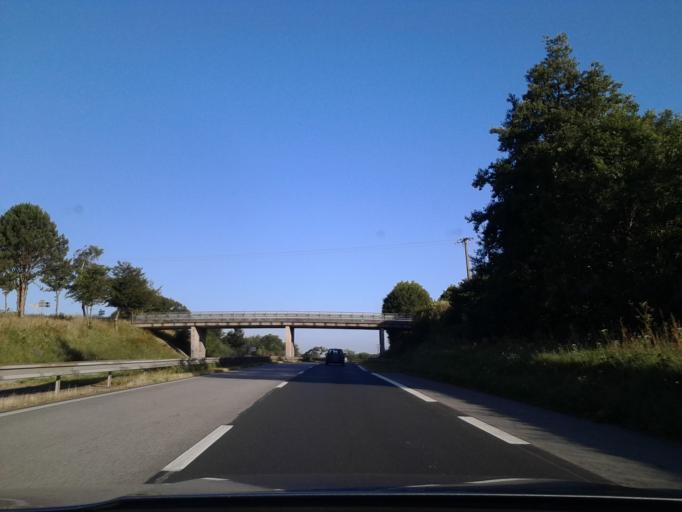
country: FR
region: Lower Normandy
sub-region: Departement de la Manche
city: Brix
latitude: 49.5333
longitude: -1.5305
